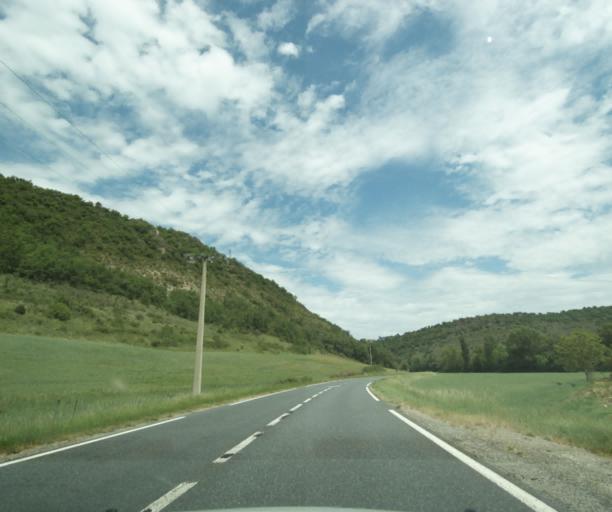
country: FR
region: Midi-Pyrenees
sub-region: Departement de l'Aveyron
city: Saint-Georges-de-Luzencon
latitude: 43.9929
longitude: 2.9677
